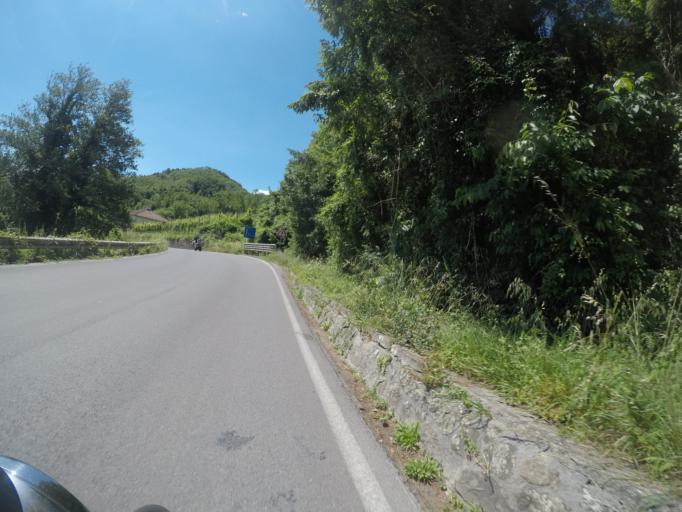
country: IT
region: Tuscany
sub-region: Provincia di Lucca
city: Castelnuovo di Garfagnana
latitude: 44.1199
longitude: 10.3936
